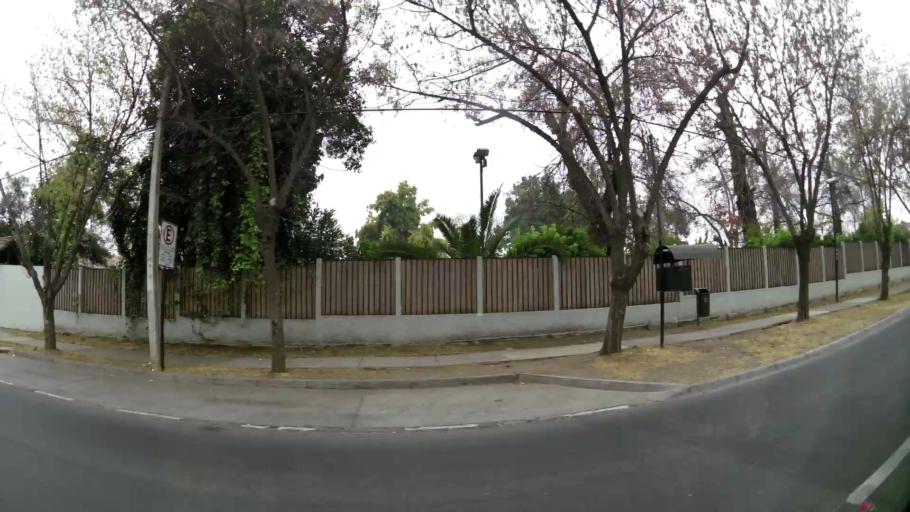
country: CL
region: Santiago Metropolitan
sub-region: Provincia de Santiago
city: Villa Presidente Frei, Nunoa, Santiago, Chile
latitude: -33.3917
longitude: -70.5635
